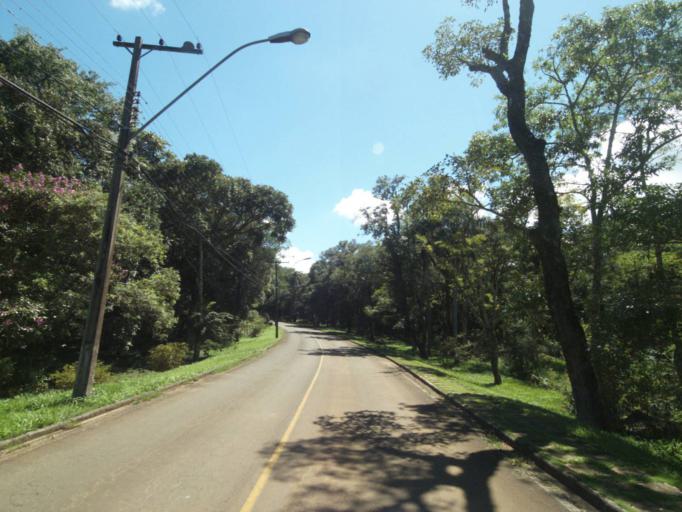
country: BR
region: Parana
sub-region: Chopinzinho
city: Chopinzinho
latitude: -25.7971
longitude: -52.0960
